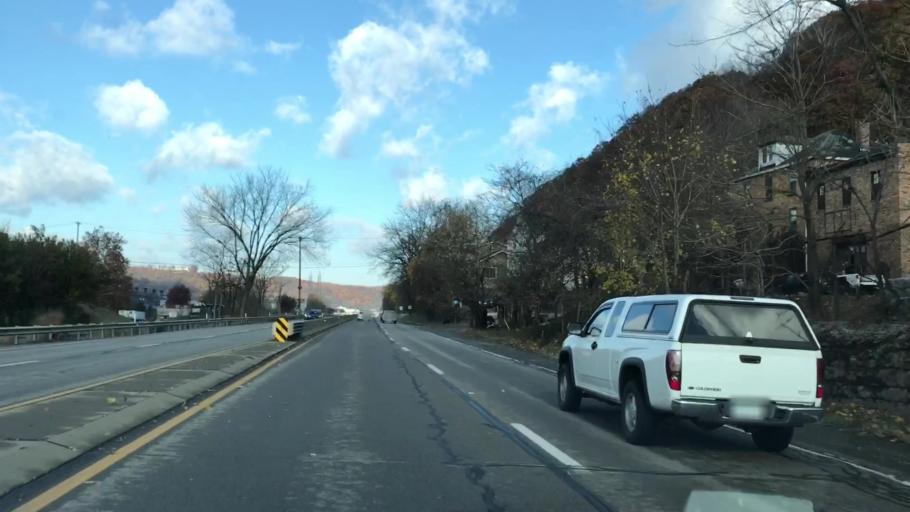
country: US
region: Pennsylvania
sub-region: Allegheny County
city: Leetsdale
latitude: 40.5700
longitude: -80.2153
